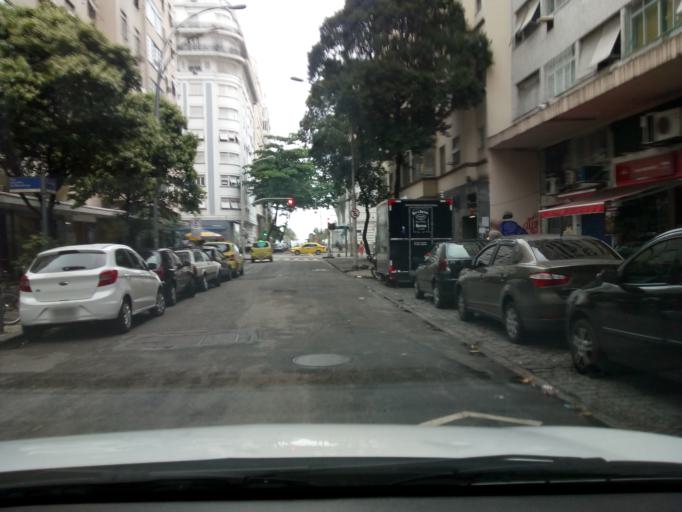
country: BR
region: Rio de Janeiro
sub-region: Rio De Janeiro
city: Rio de Janeiro
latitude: -22.9657
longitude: -43.1791
